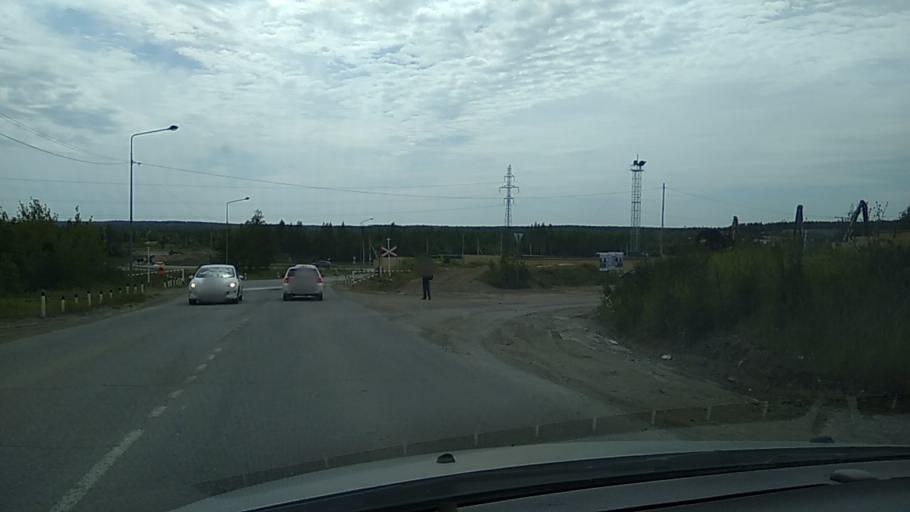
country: RU
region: Sverdlovsk
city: Verkhnyaya Pyshma
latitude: 56.9539
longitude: 60.5863
